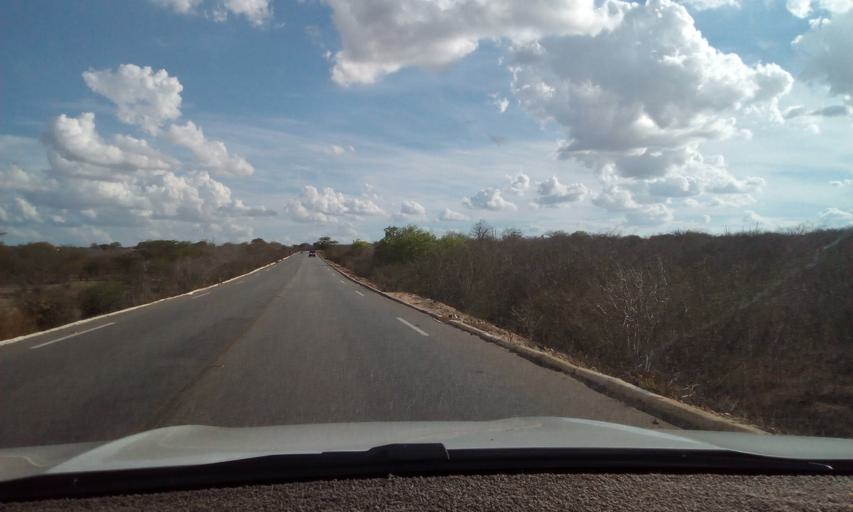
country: BR
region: Paraiba
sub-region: Soledade
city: Soledade
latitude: -6.9154
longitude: -36.3860
